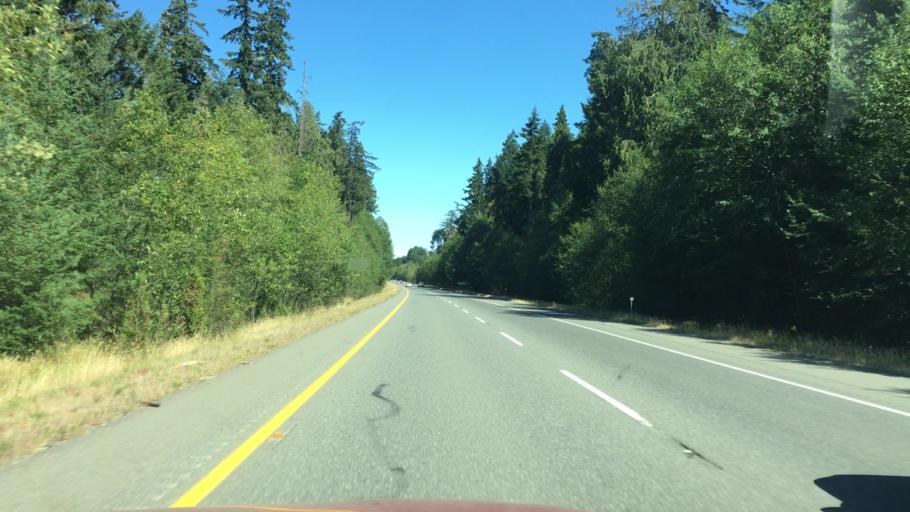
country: CA
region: British Columbia
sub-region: Regional District of Nanaimo
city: Parksville
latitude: 49.3173
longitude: -124.3864
